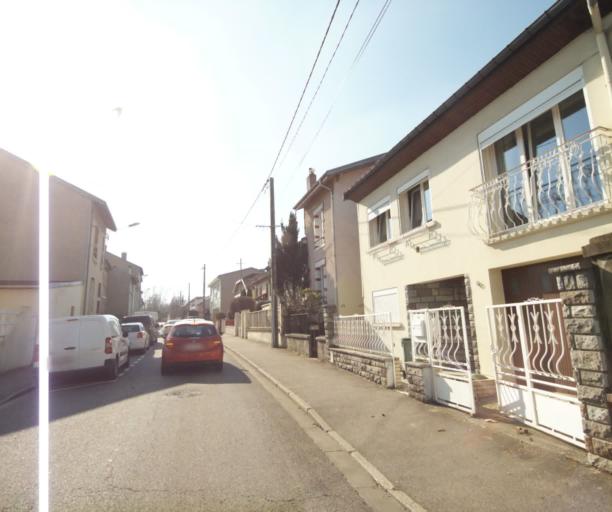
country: FR
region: Lorraine
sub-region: Departement de Meurthe-et-Moselle
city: Jarville-la-Malgrange
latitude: 48.6670
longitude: 6.1994
